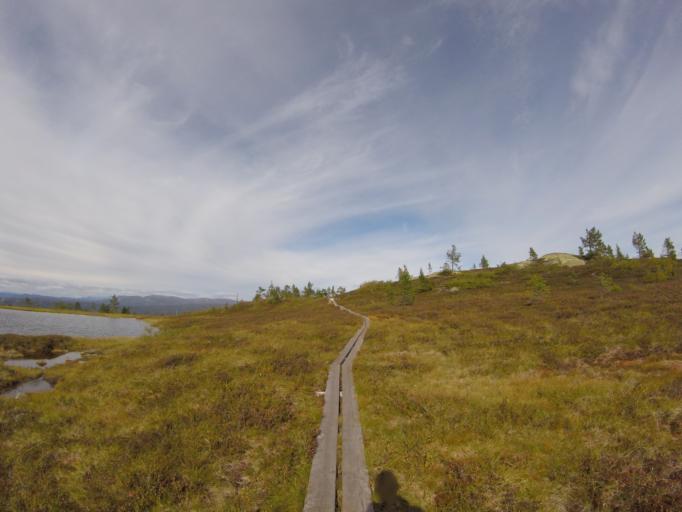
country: NO
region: Buskerud
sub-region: Flesberg
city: Lampeland
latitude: 59.7493
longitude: 9.4184
